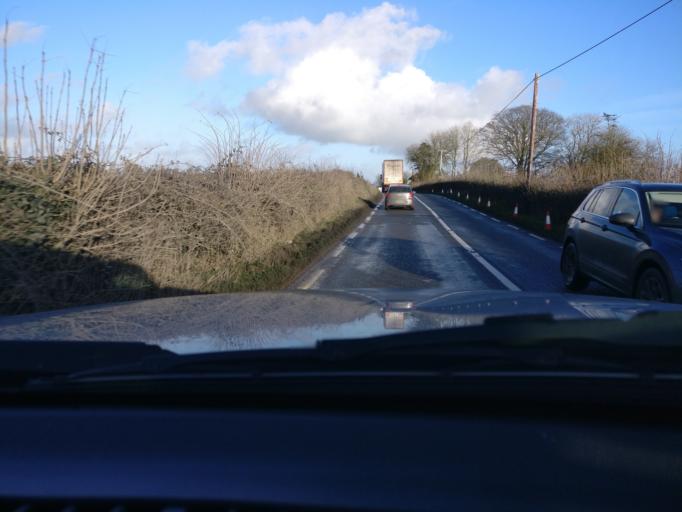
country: IE
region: Leinster
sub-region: An Iarmhi
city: Rathwire
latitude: 53.5819
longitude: -7.1424
